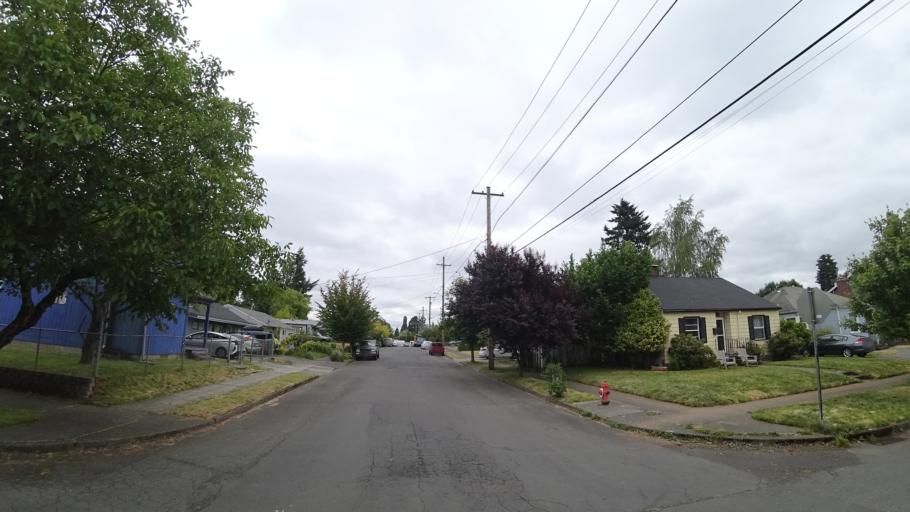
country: US
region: Oregon
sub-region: Multnomah County
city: Lents
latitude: 45.5115
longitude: -122.5812
